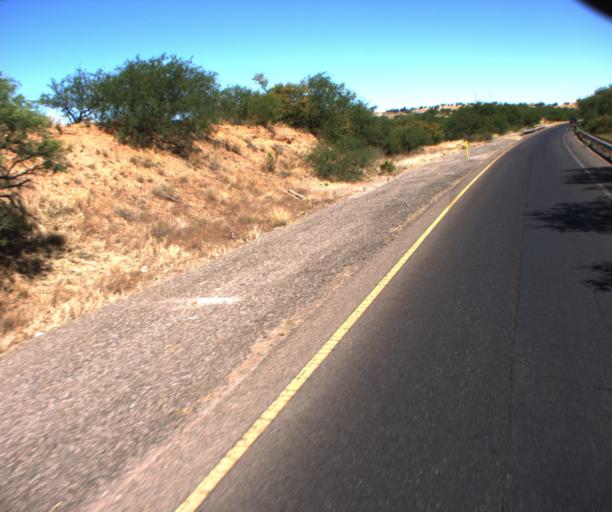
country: US
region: Arizona
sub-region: Santa Cruz County
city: Nogales
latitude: 31.3959
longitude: -110.9580
